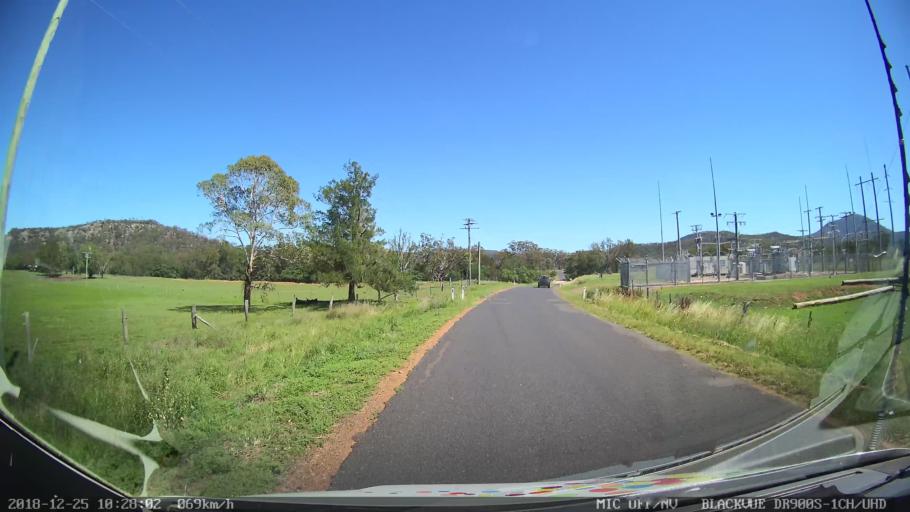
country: AU
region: New South Wales
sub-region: Muswellbrook
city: Denman
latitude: -32.3856
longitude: 150.4665
